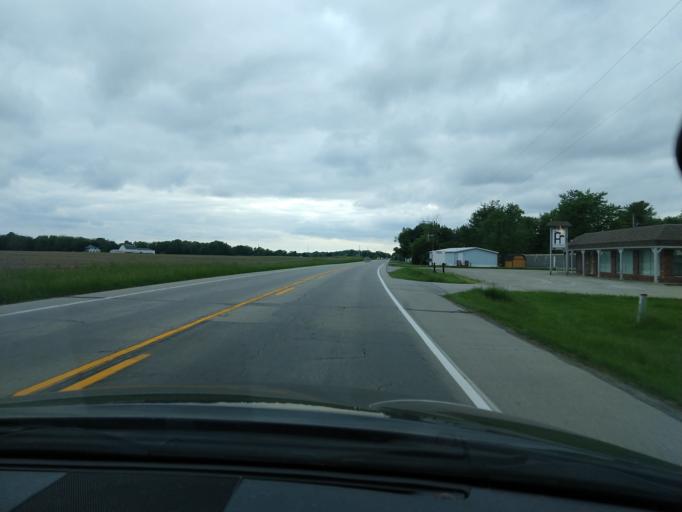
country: US
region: Indiana
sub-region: Madison County
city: Lapel
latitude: 40.0549
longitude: -85.9154
